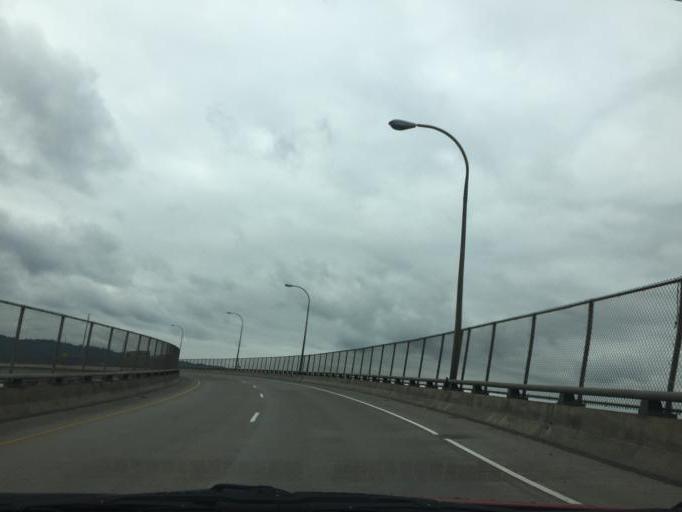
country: US
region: Oregon
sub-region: Multnomah County
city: Portland
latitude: 45.5434
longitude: -122.6743
